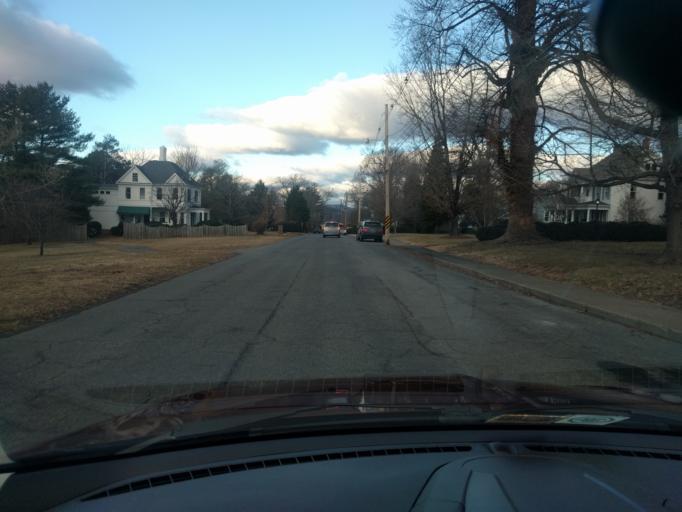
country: US
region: Virginia
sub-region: City of Bedford
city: Bedford
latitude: 37.3404
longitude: -79.5261
